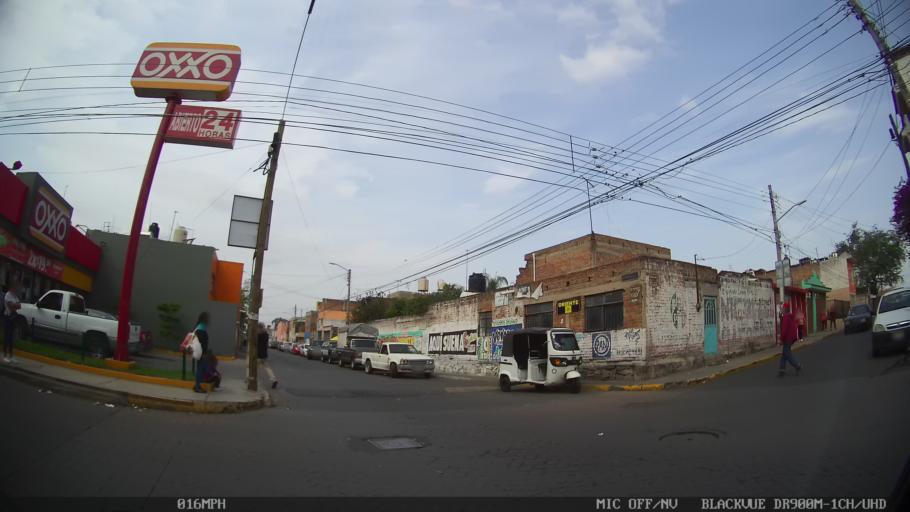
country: MX
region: Jalisco
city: Tonala
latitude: 20.6212
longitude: -103.2373
